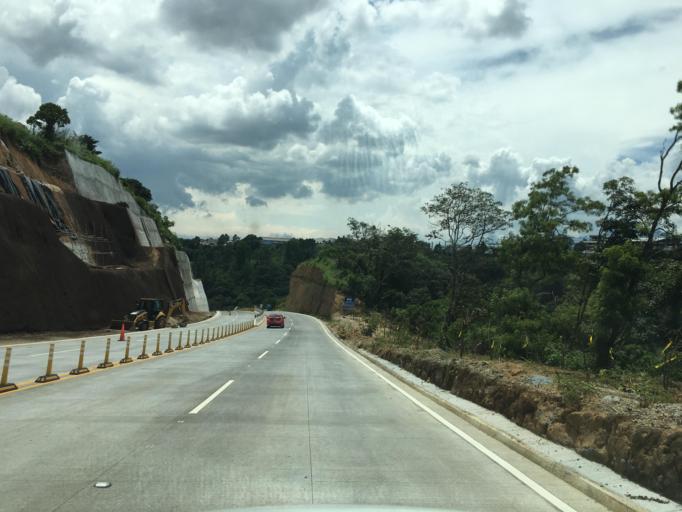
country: GT
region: Guatemala
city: Santa Catarina Pinula
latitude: 14.5702
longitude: -90.5379
